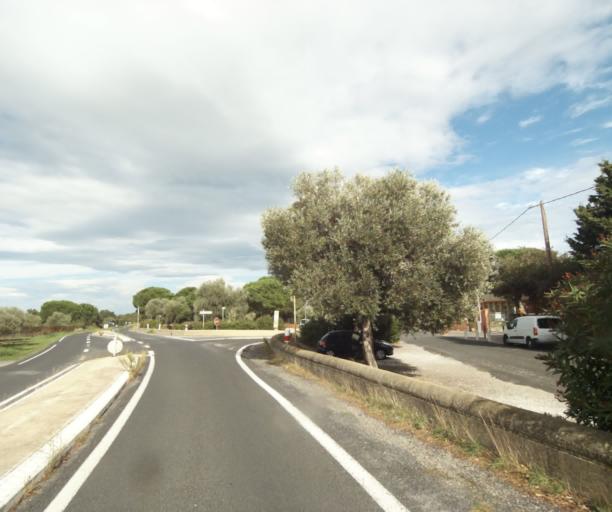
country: FR
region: Languedoc-Roussillon
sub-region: Departement des Pyrenees-Orientales
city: Sant Andreu de Sureda
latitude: 42.5349
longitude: 2.9940
